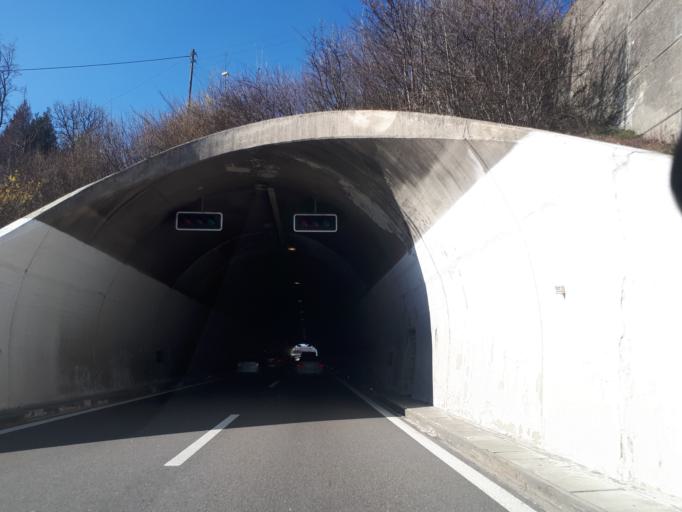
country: CH
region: Vaud
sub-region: Lavaux-Oron District
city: Cully
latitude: 46.5005
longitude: 6.7174
